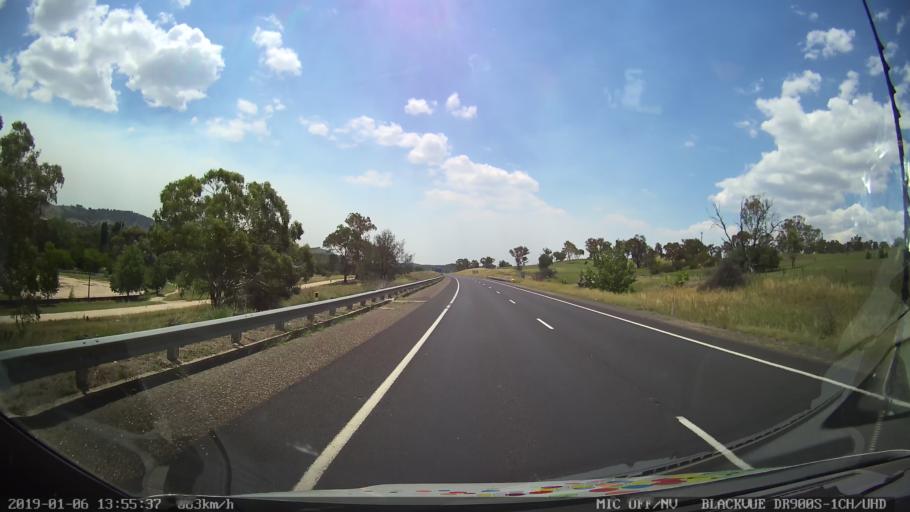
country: AU
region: New South Wales
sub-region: Tamworth Municipality
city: Kootingal
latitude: -30.8862
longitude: 151.1588
